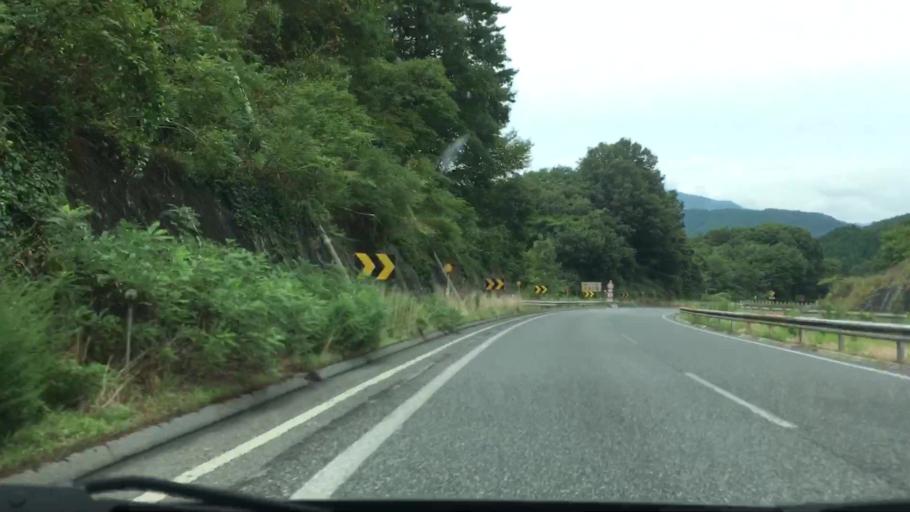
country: JP
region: Okayama
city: Niimi
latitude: 35.0145
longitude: 133.5849
